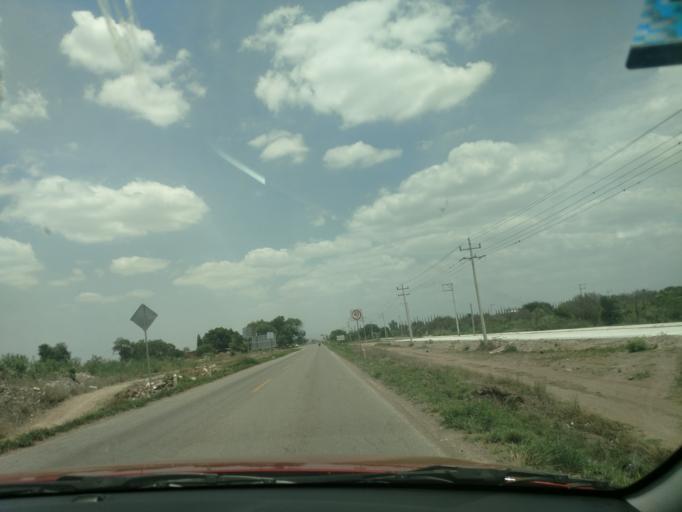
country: MX
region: San Luis Potosi
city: Ciudad Fernandez
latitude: 21.9438
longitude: -100.0467
